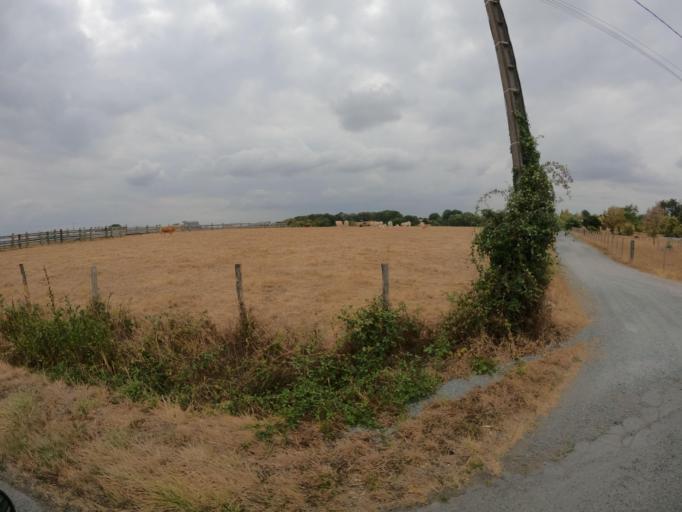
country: FR
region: Pays de la Loire
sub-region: Departement de Maine-et-Loire
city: Le Longeron
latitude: 47.0252
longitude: -1.0510
